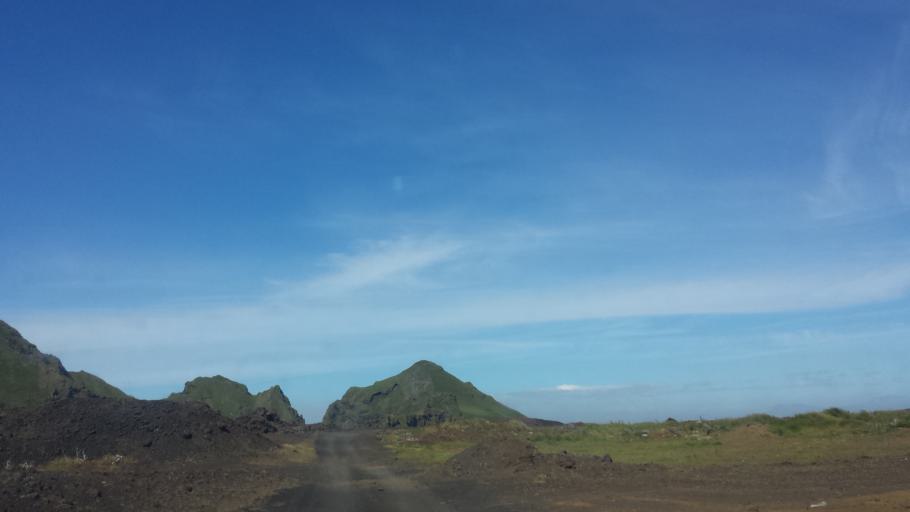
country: IS
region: South
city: Vestmannaeyjar
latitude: 63.4381
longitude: -20.2453
